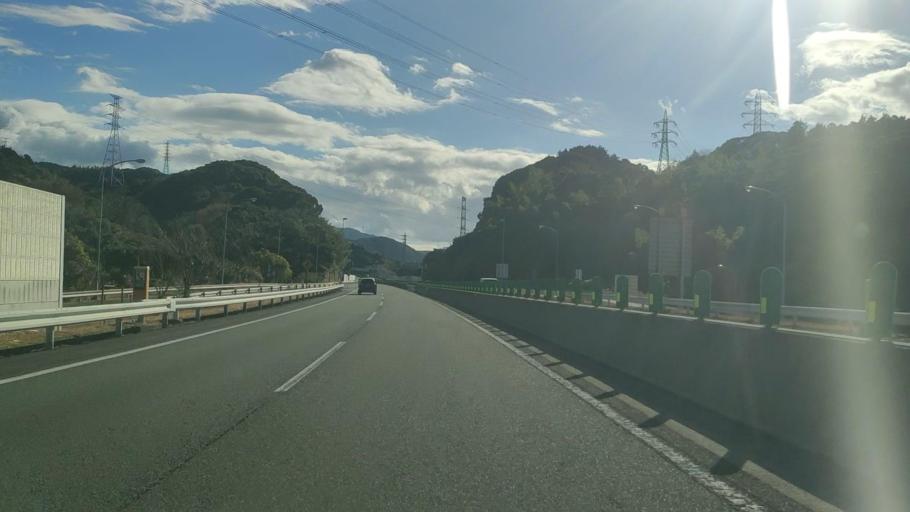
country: JP
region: Fukuoka
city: Kitakyushu
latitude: 33.8405
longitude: 130.7654
